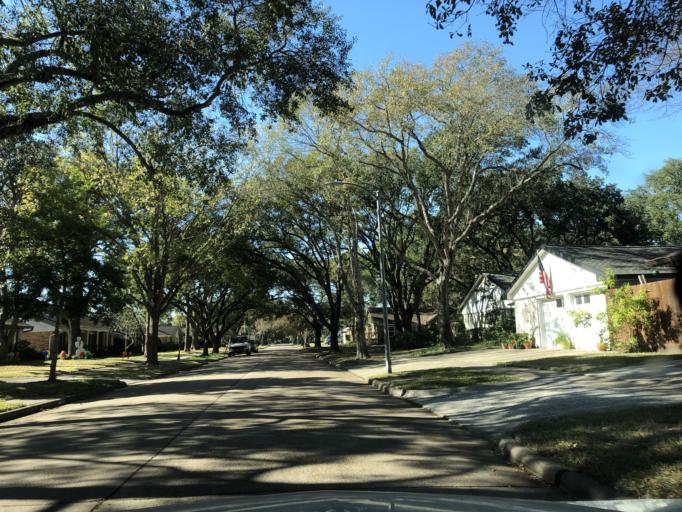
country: US
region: Texas
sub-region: Harris County
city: Bellaire
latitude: 29.6760
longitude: -95.4975
